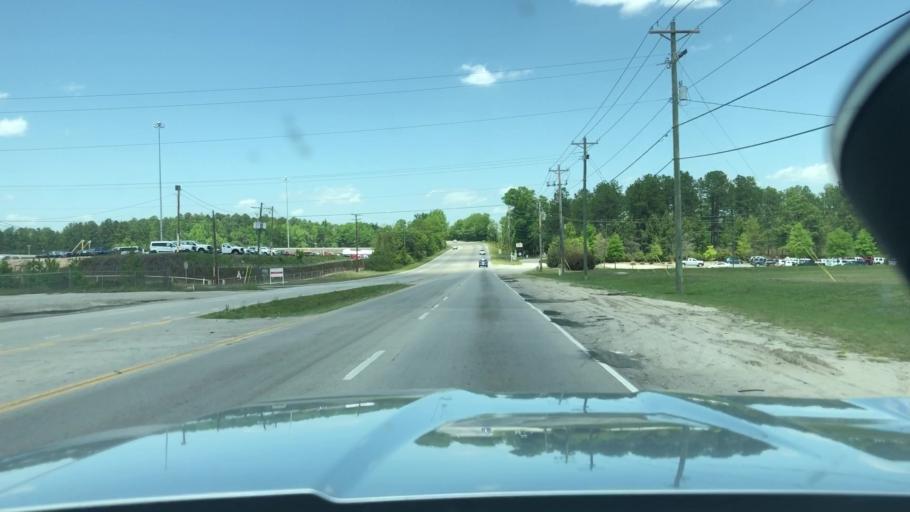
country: US
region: South Carolina
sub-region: Lexington County
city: Pineridge
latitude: 33.9040
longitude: -81.0651
